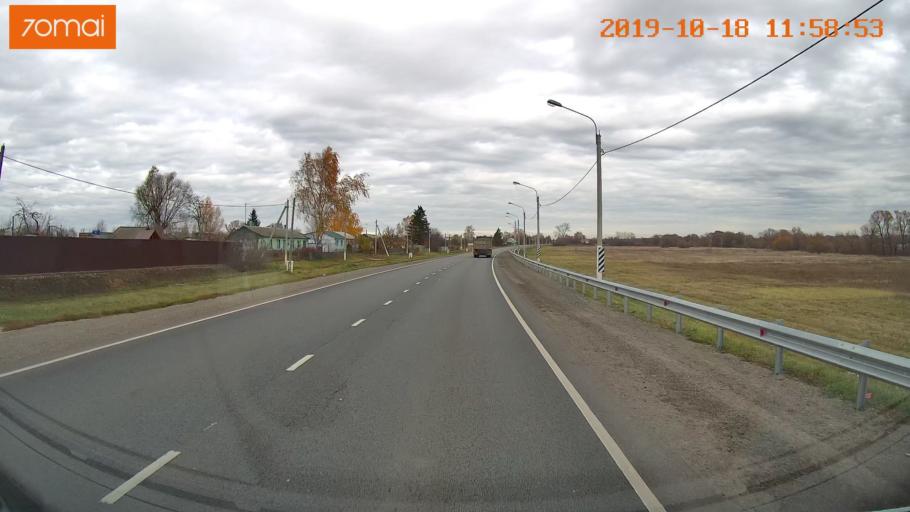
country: RU
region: Rjazan
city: Zakharovo
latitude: 54.2763
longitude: 39.1705
